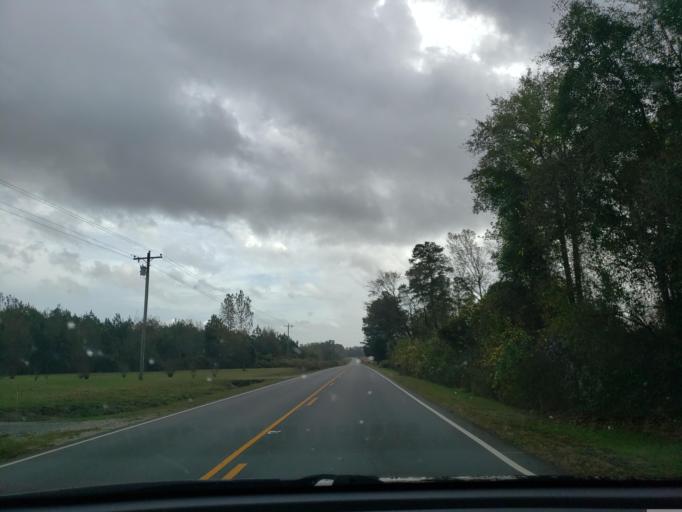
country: US
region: North Carolina
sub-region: Duplin County
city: Beulaville
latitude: 34.8467
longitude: -77.8693
